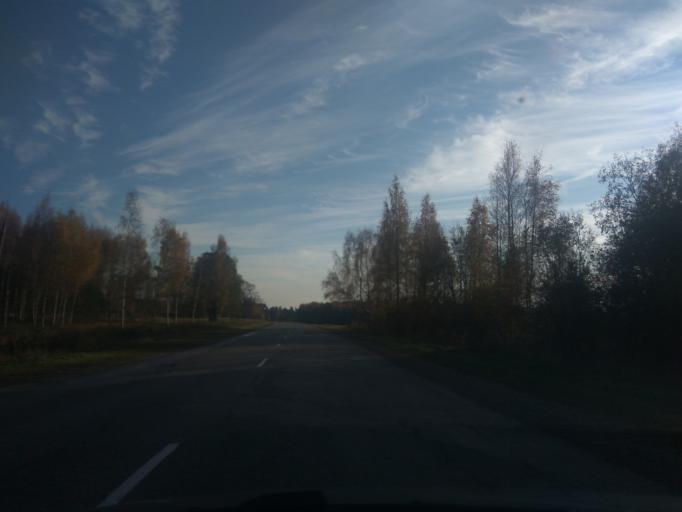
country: LV
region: Ventspils
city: Ventspils
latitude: 57.2948
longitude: 21.5634
